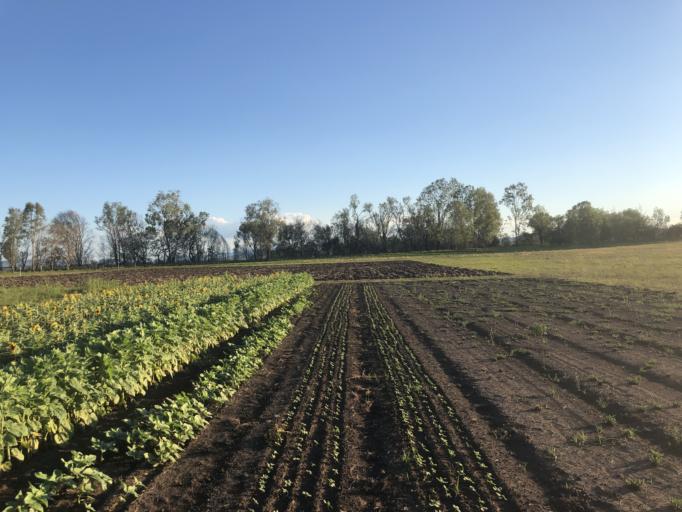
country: AU
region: Queensland
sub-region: Lockyer Valley
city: Gatton
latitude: -27.5882
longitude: 152.3446
